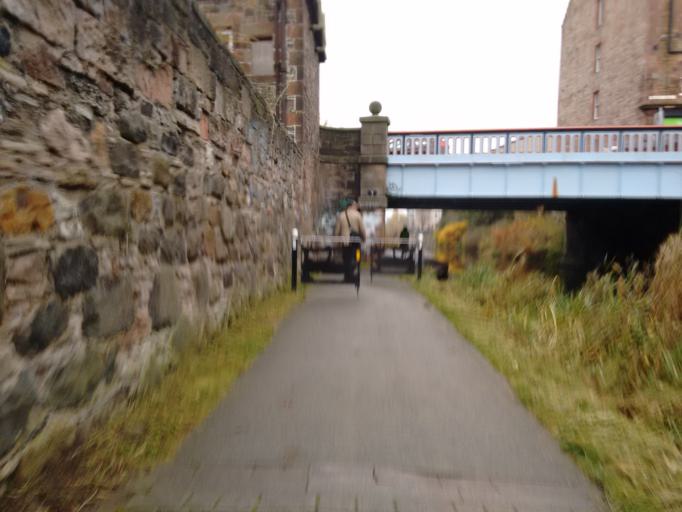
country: GB
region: Scotland
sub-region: Edinburgh
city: Edinburgh
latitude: 55.9386
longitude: -3.2187
